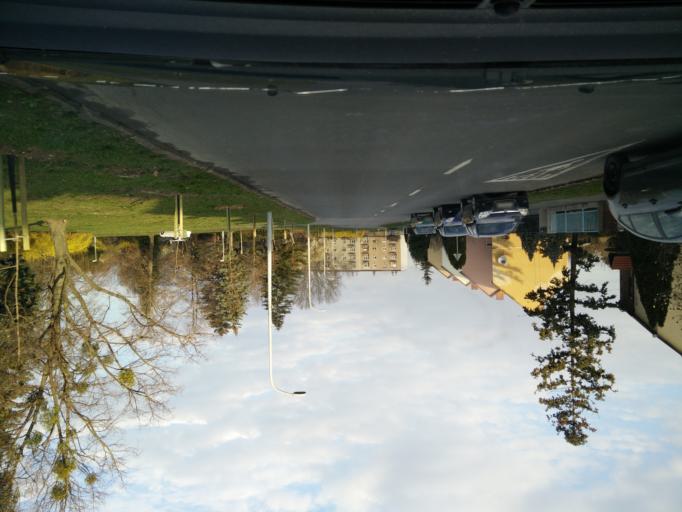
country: HU
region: Zala
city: Zalaegerszeg
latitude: 46.8414
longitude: 16.8384
